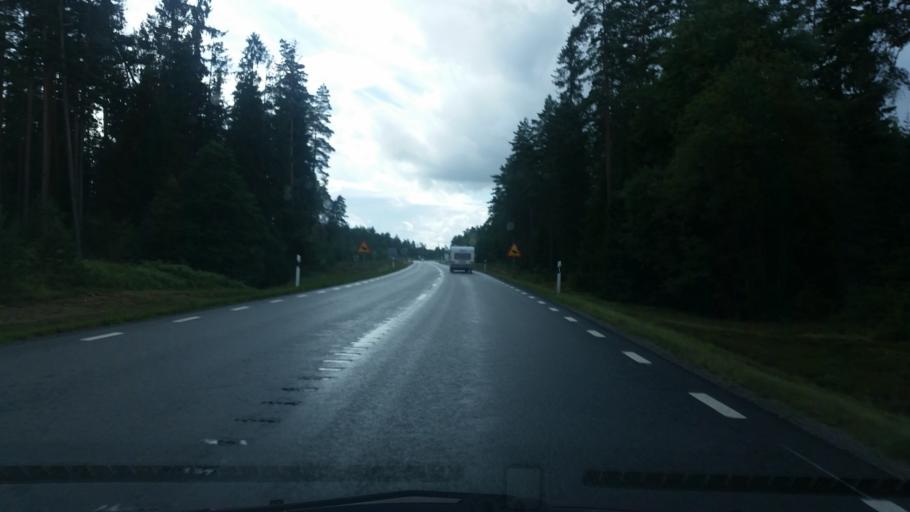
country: SE
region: Joenkoeping
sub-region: Gislaveds Kommun
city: Gislaved
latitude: 57.3541
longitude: 13.5581
